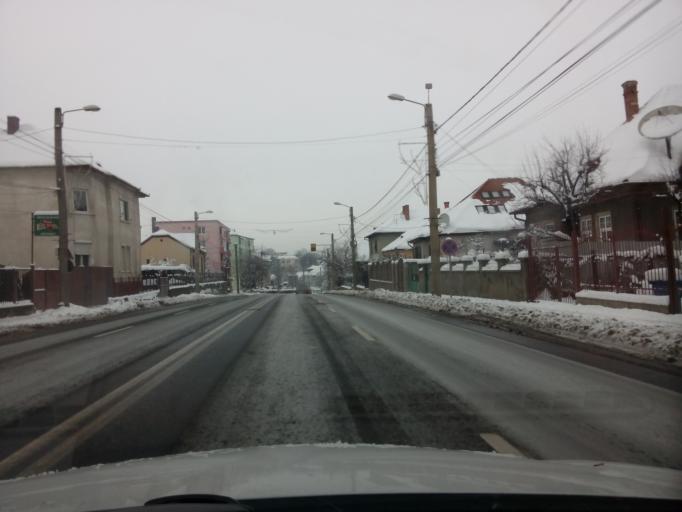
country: RO
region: Sibiu
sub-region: Municipiul Sibiu
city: Sibiu
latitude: 45.7925
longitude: 24.1618
